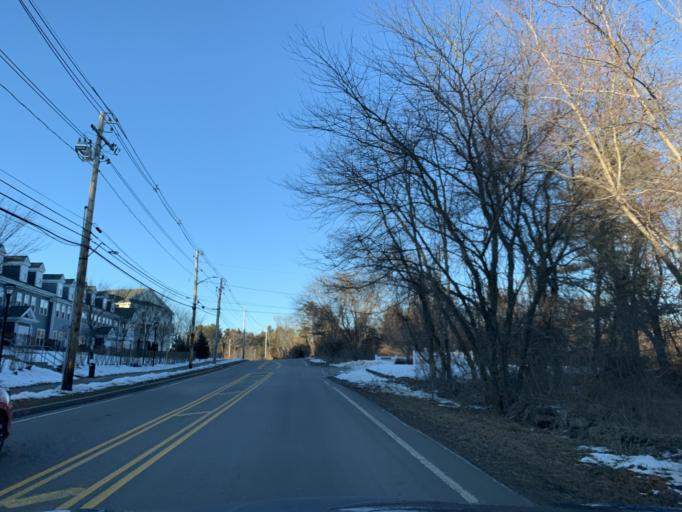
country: US
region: Massachusetts
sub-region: Bristol County
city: Norton Center
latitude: 41.9876
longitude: -71.1559
